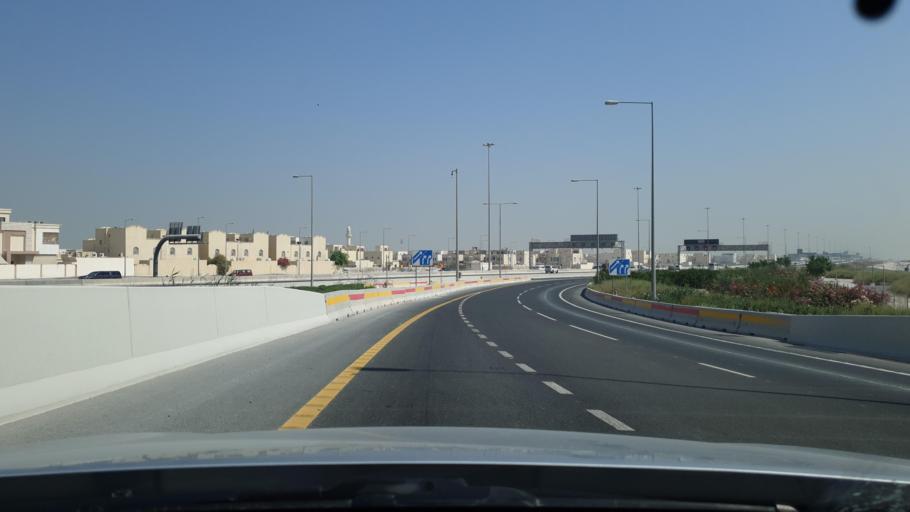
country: QA
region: Baladiyat ad Dawhah
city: Doha
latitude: 25.2209
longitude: 51.5375
